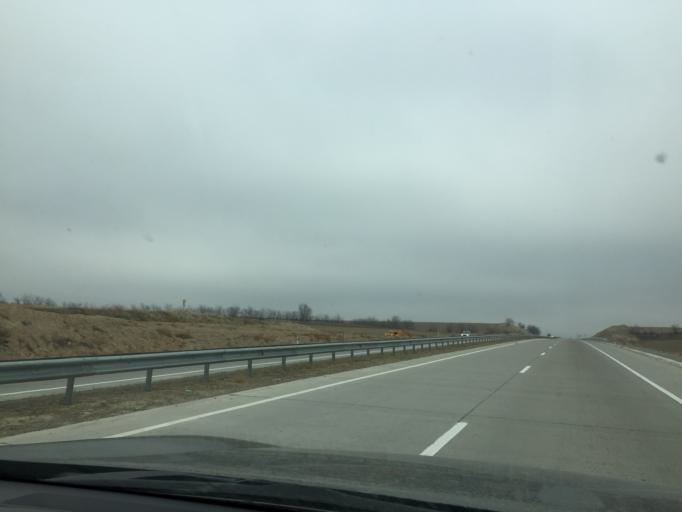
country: KZ
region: Ongtustik Qazaqstan
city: Aksu
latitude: 42.4757
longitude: 69.8891
